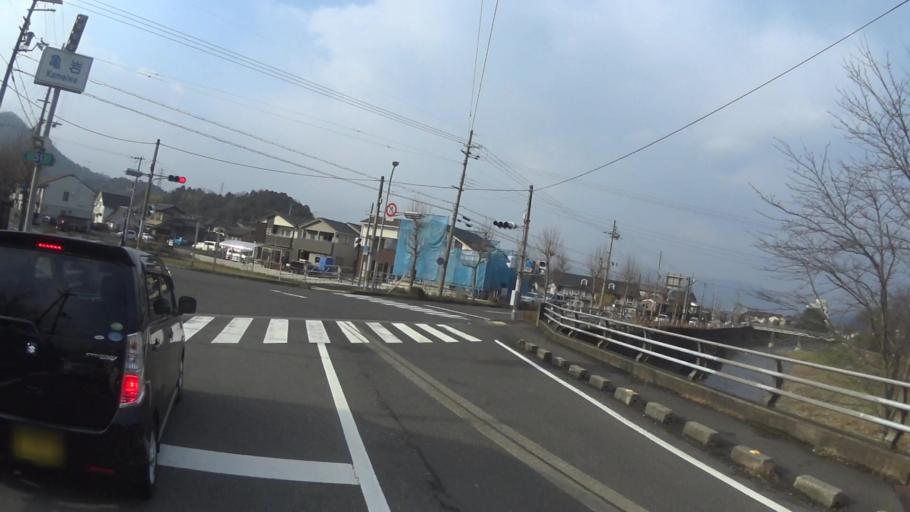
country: JP
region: Kyoto
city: Maizuru
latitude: 35.4497
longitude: 135.4083
